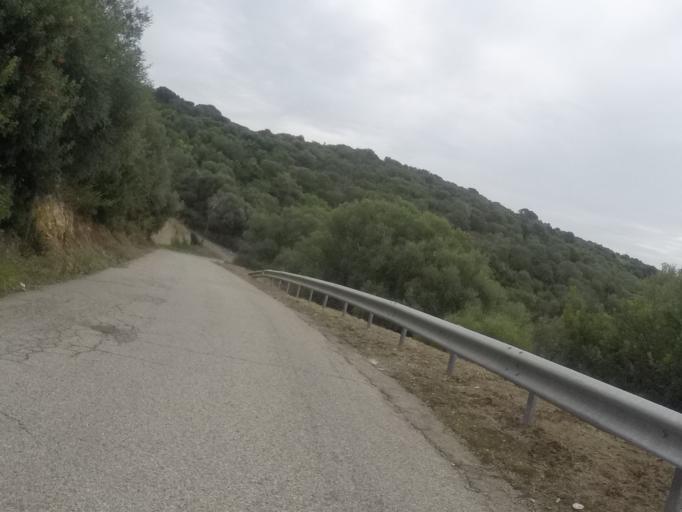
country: FR
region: Corsica
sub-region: Departement de la Corse-du-Sud
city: Pietrosella
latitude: 41.7594
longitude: 8.8127
